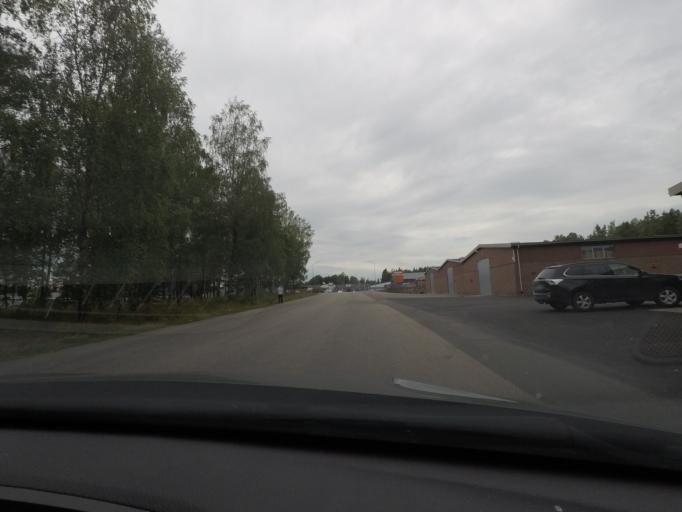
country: SE
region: Skane
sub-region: Osby Kommun
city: Osby
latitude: 56.3833
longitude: 13.9770
